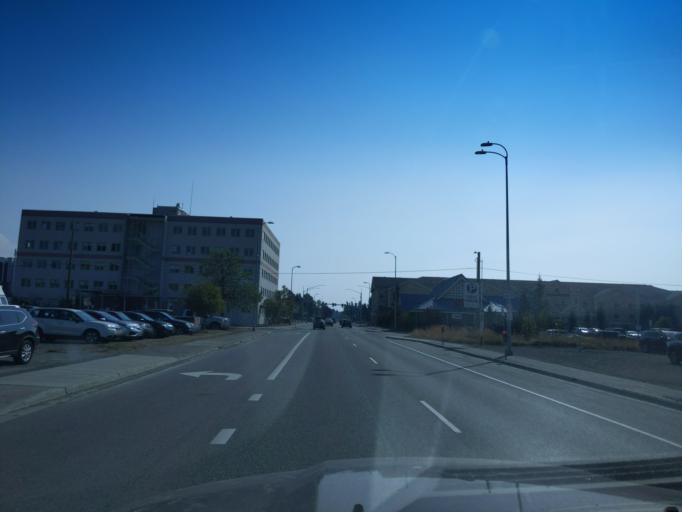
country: US
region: Alaska
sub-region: Anchorage Municipality
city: Anchorage
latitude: 61.2152
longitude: -149.9037
